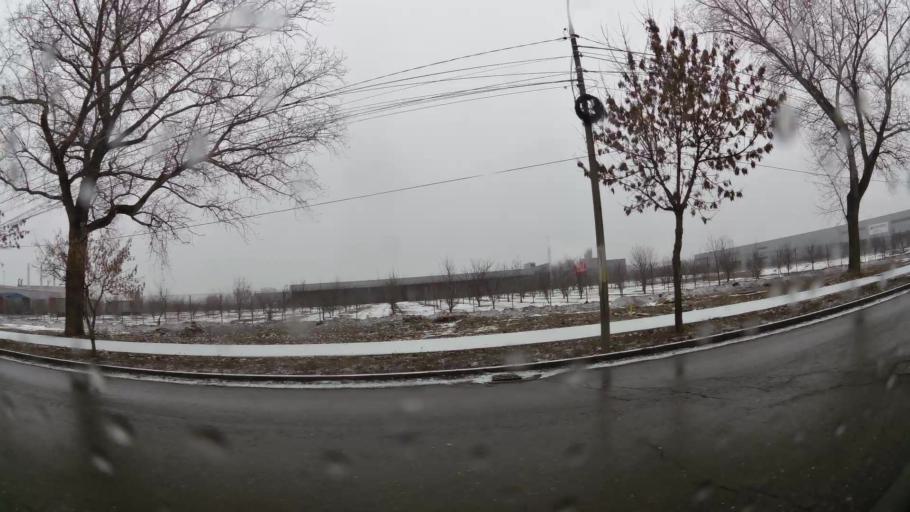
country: RO
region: Dambovita
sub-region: Municipiul Targoviste
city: Targoviste
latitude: 44.9198
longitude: 25.4358
